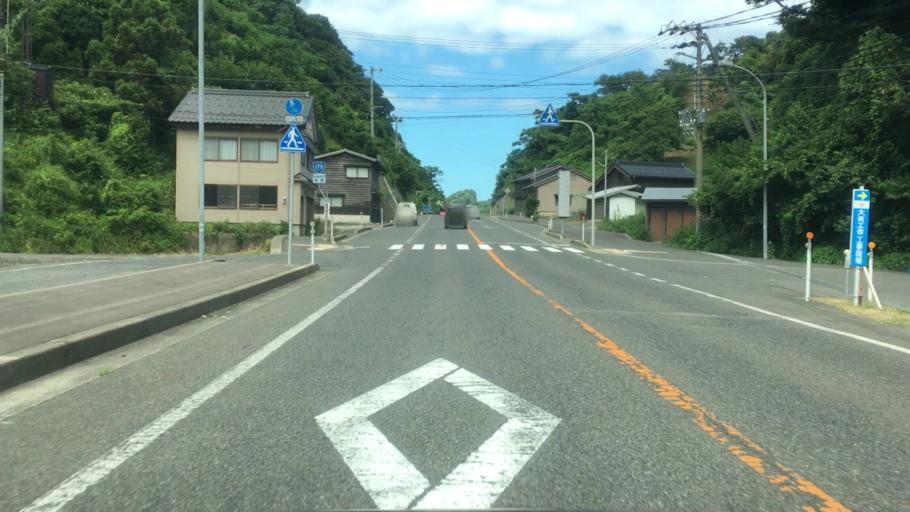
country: JP
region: Tottori
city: Tottori
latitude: 35.6169
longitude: 134.4111
